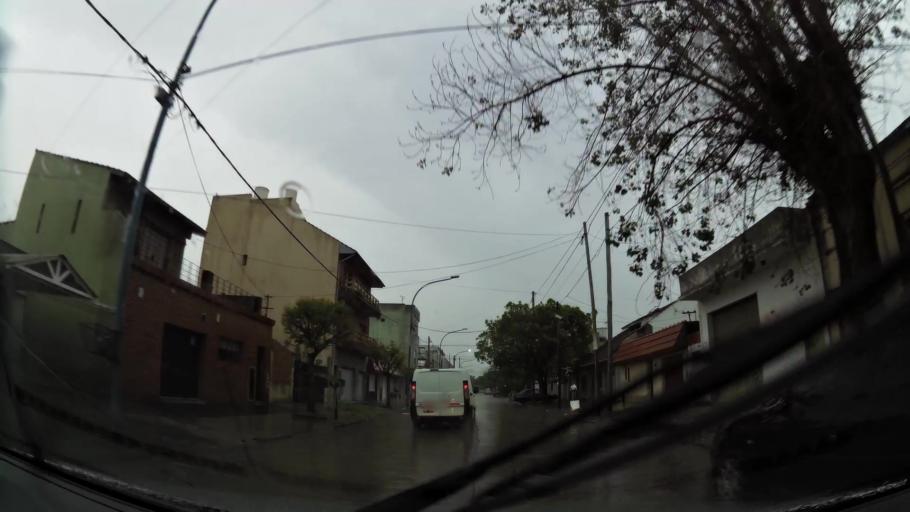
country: AR
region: Buenos Aires
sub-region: Partido de Lanus
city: Lanus
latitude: -34.7116
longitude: -58.4052
